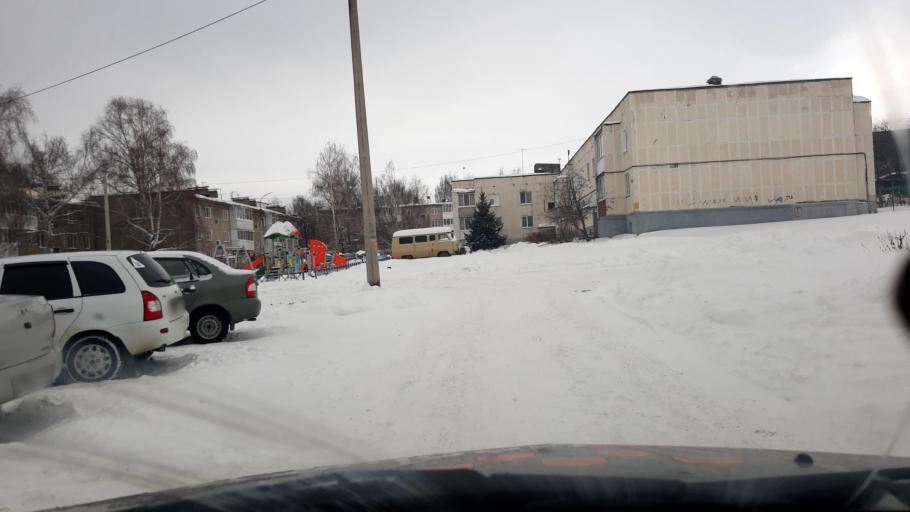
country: RU
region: Bashkortostan
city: Avdon
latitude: 54.6688
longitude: 55.7169
